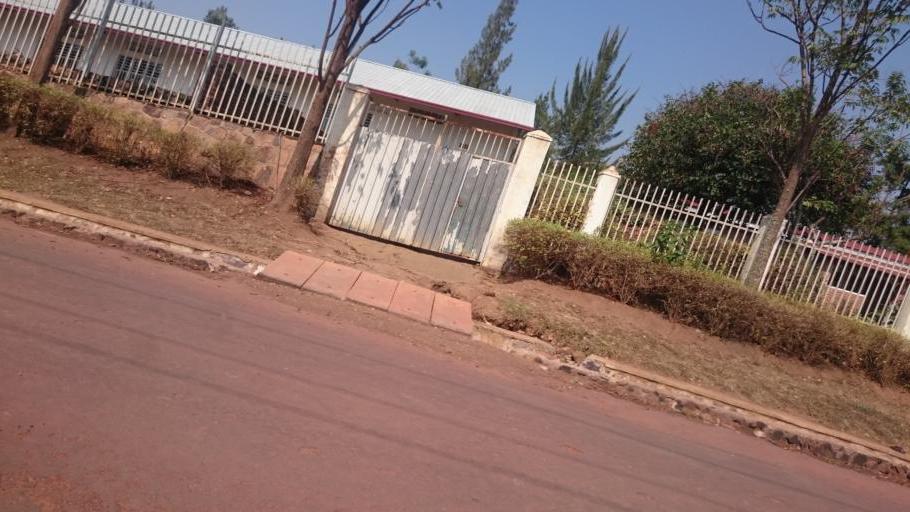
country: RW
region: Kigali
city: Kigali
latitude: -1.9413
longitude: 30.0887
